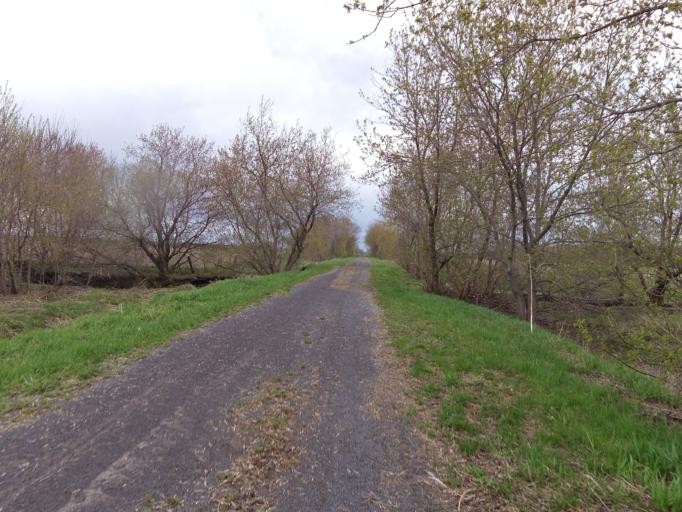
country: CA
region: Quebec
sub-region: Outaouais
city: Papineauville
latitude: 45.5226
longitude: -74.9100
